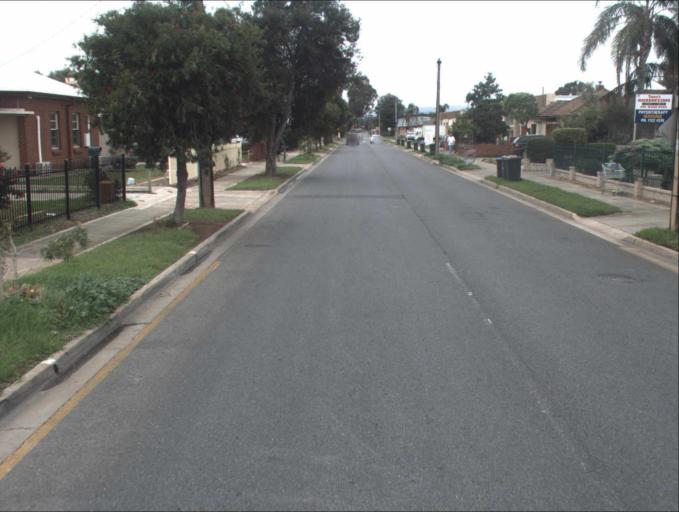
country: AU
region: South Australia
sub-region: Charles Sturt
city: Woodville North
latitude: -34.8722
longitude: 138.5523
